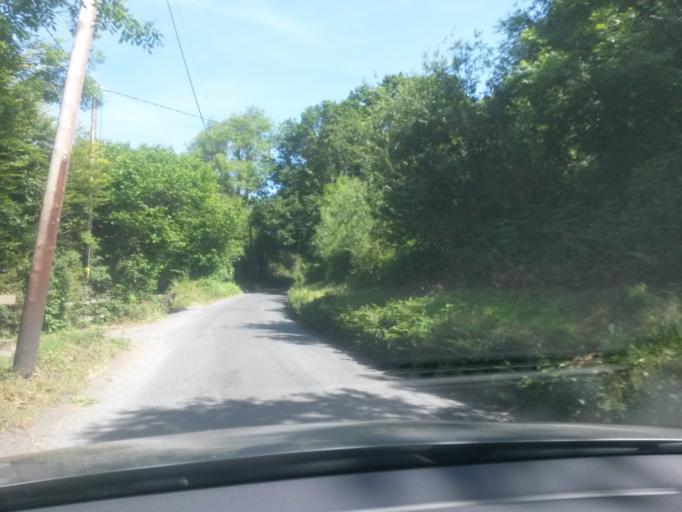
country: IE
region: Leinster
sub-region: Wicklow
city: Enniskerry
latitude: 53.1596
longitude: -6.1938
